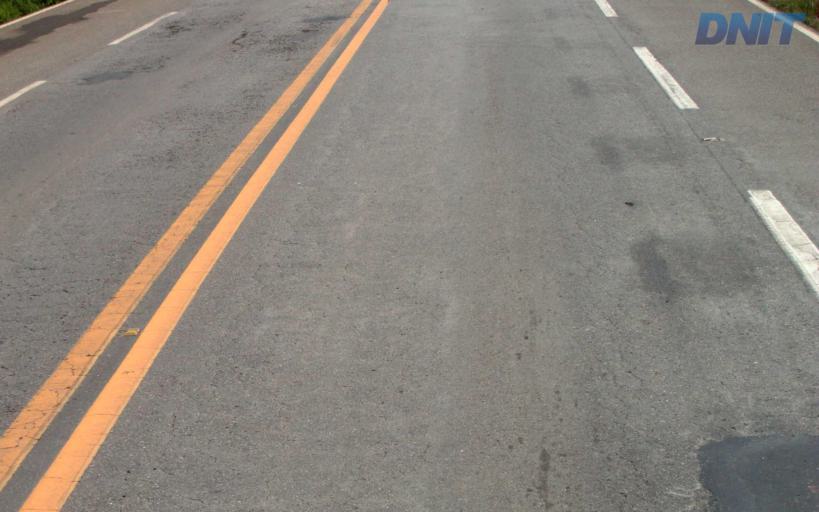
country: BR
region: Minas Gerais
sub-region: Governador Valadares
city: Governador Valadares
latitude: -19.0711
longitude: -42.1759
